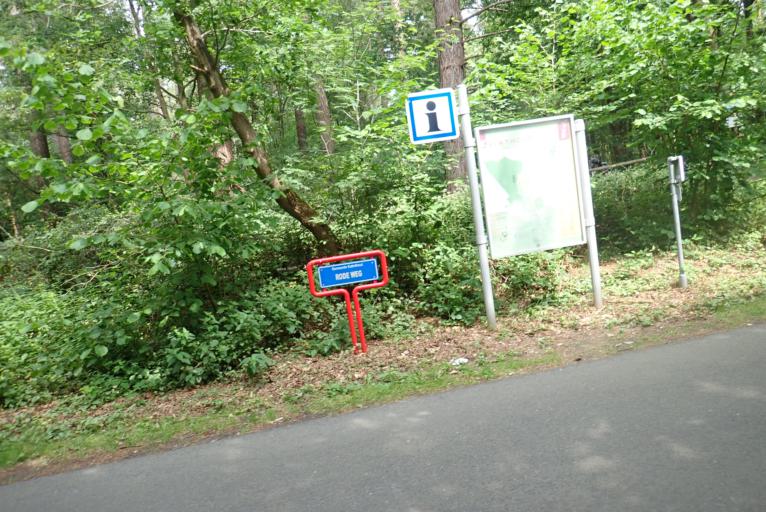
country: BE
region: Flanders
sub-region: Provincie Antwerpen
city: Kalmthout
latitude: 51.3634
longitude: 4.4809
